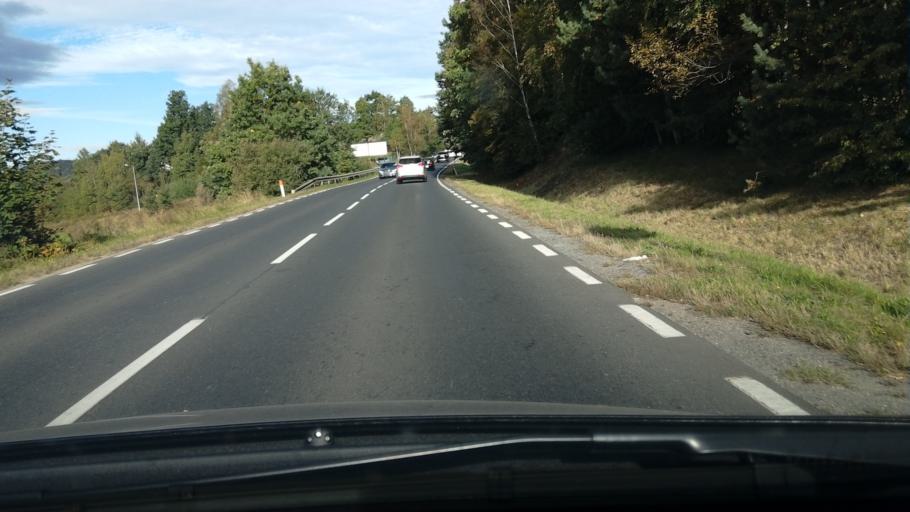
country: PL
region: Lower Silesian Voivodeship
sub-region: Powiat jeleniogorski
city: Myslakowice
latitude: 50.8717
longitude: 15.7629
